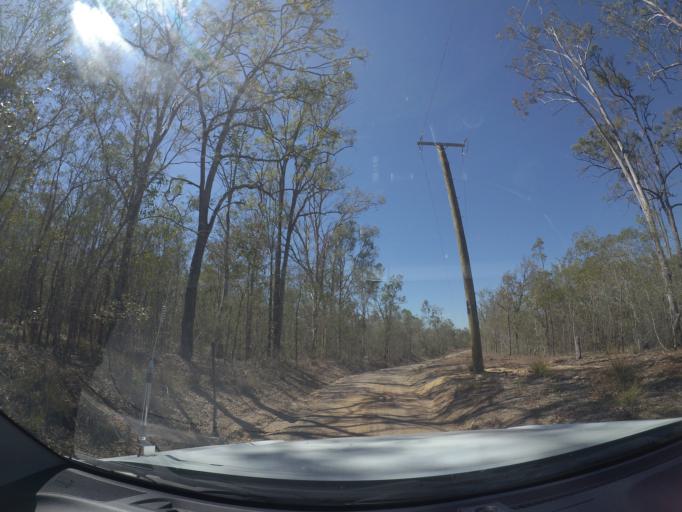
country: AU
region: Queensland
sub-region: Logan
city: North Maclean
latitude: -27.7691
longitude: 152.9368
